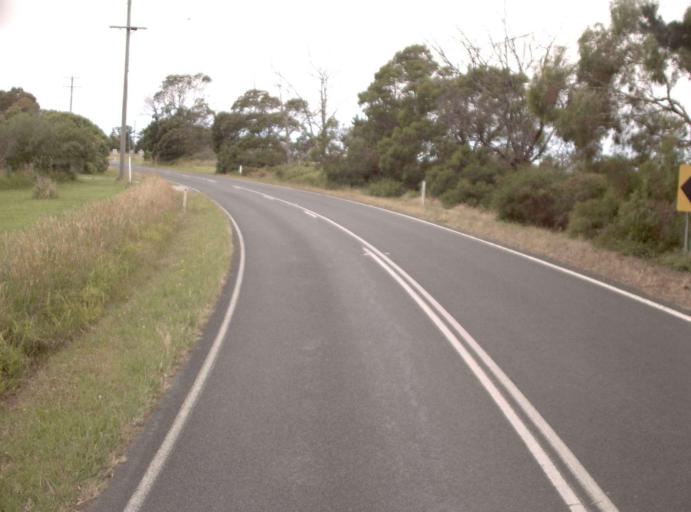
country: AU
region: Victoria
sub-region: Wellington
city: Sale
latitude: -38.5308
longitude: 146.8770
